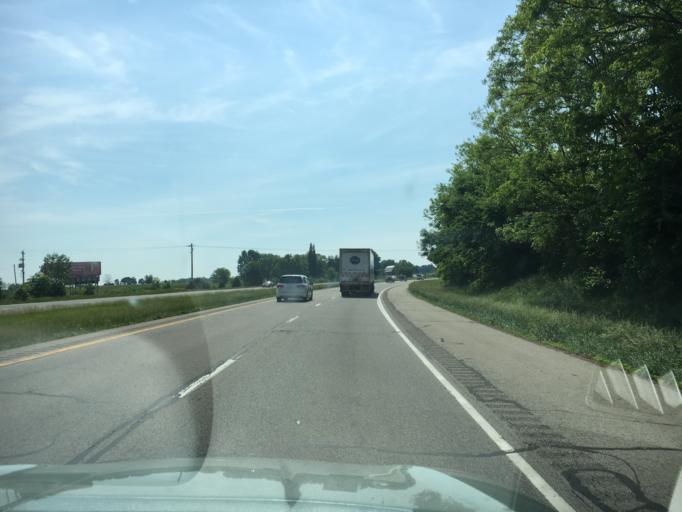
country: US
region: Indiana
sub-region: Ripley County
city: Sunman
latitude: 39.2877
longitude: -84.9775
